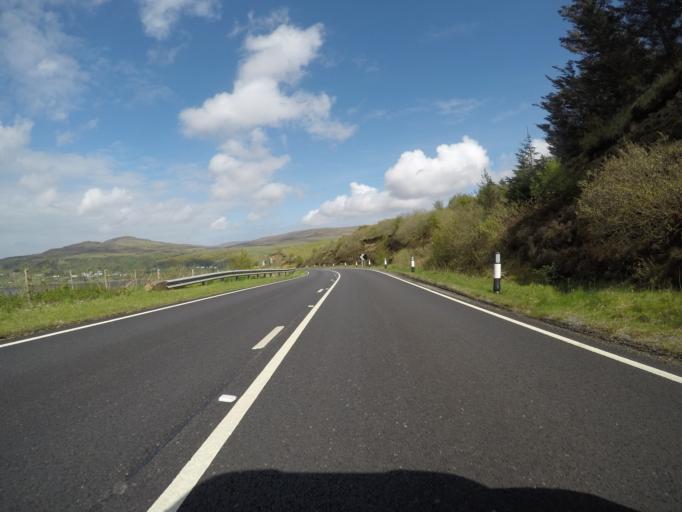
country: GB
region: Scotland
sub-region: Highland
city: Portree
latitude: 57.5784
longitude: -6.3639
